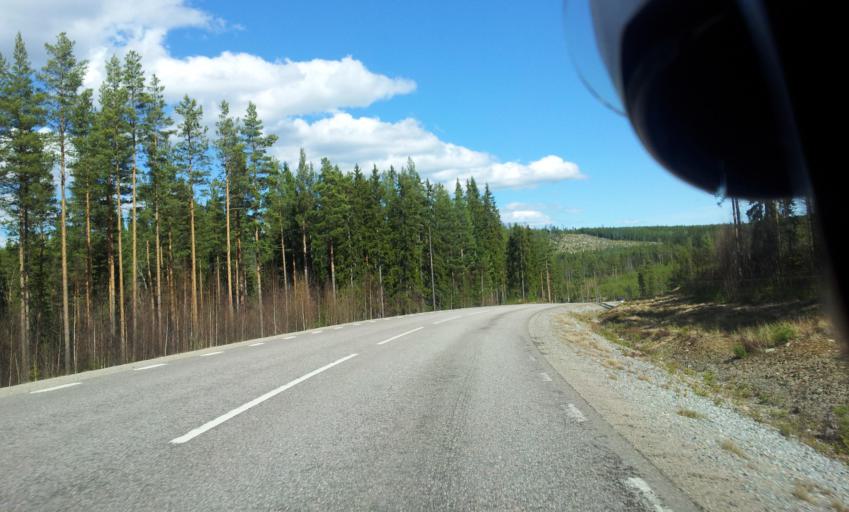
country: SE
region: Gaevleborg
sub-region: Ovanakers Kommun
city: Edsbyn
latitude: 61.2271
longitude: 15.8777
